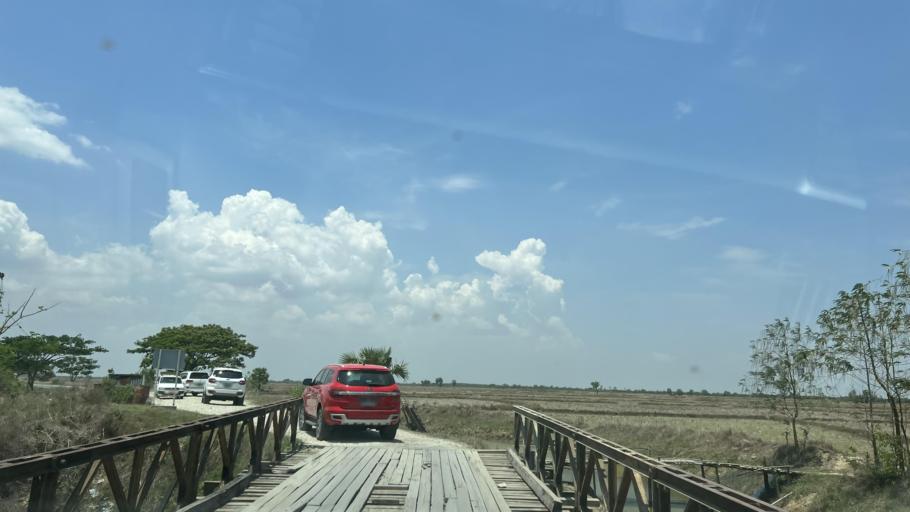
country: MM
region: Ayeyarwady
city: Pyapon
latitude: 15.9139
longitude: 95.6005
